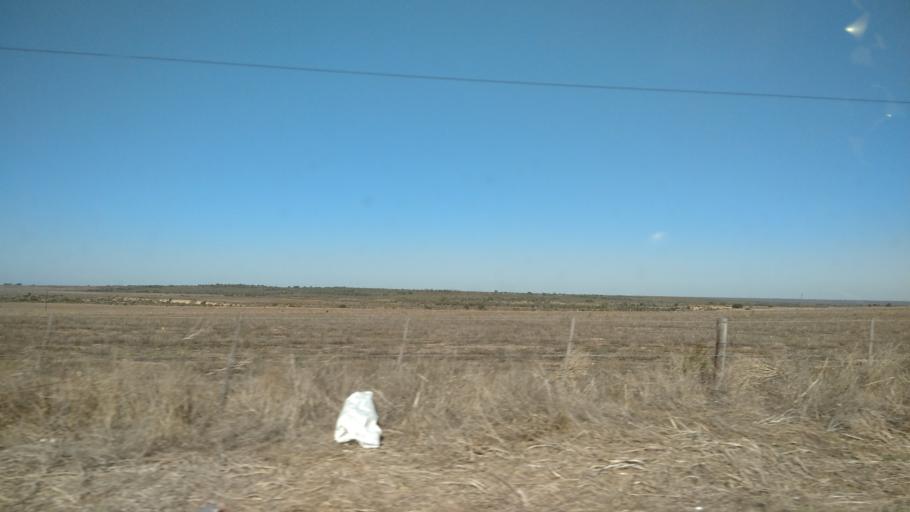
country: ZA
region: Western Cape
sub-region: West Coast District Municipality
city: Moorreesburg
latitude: -33.1094
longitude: 18.4304
